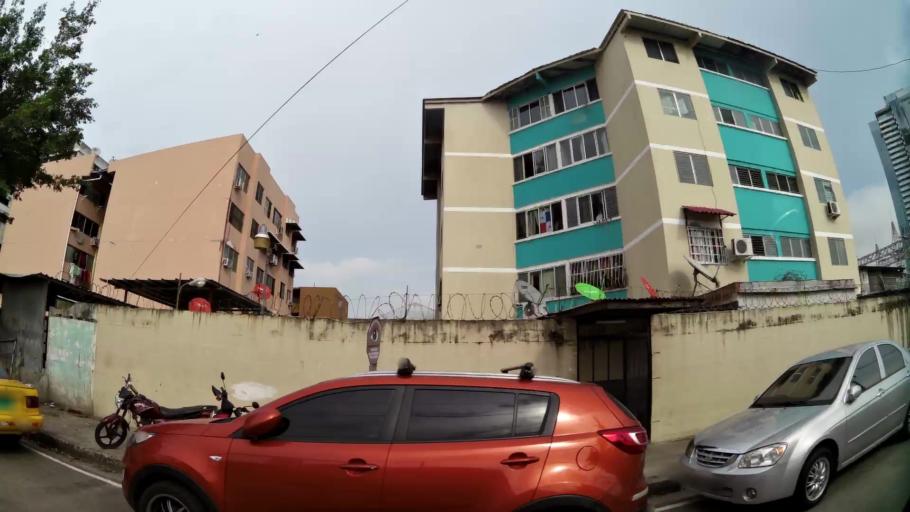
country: PA
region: Panama
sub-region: Distrito de Panama
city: Ancon
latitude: 8.9616
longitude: -79.5374
